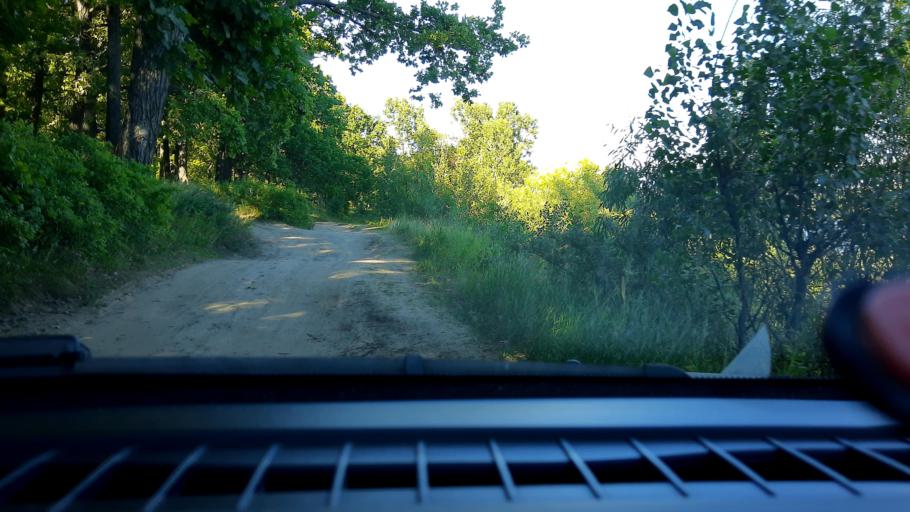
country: RU
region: Nizjnij Novgorod
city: Burevestnik
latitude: 56.2009
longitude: 43.8276
